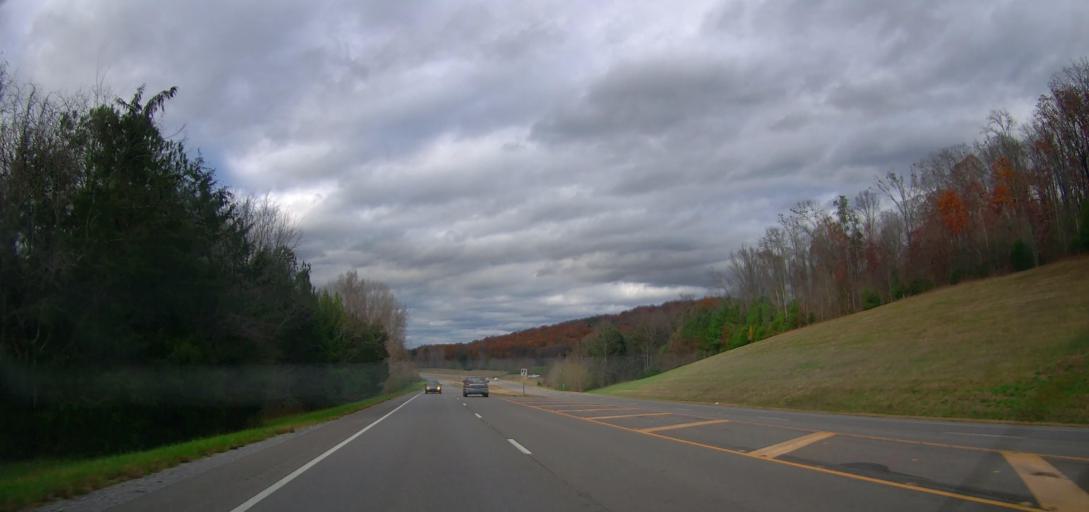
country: US
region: Alabama
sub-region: Morgan County
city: Falkville
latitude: 34.3213
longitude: -87.0009
